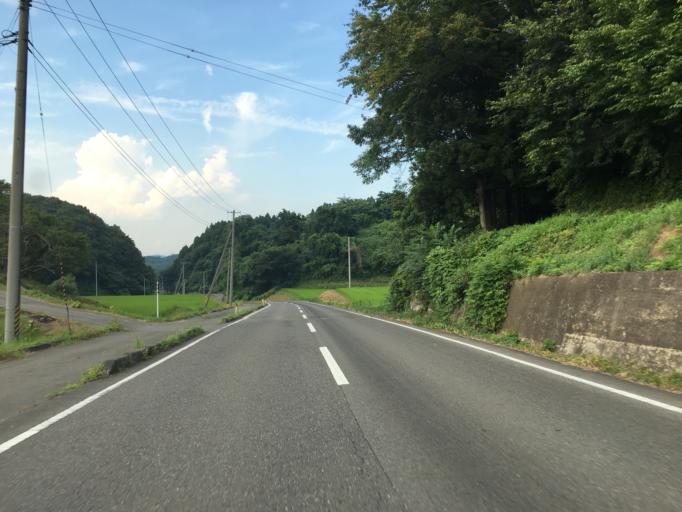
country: JP
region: Fukushima
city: Motomiya
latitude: 37.5361
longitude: 140.4415
